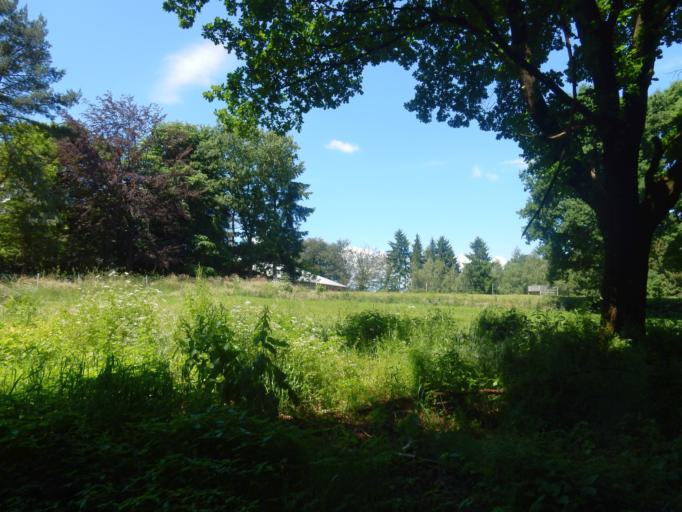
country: LU
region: Luxembourg
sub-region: Canton de Mersch
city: Tuntange
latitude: 49.7444
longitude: 6.0191
